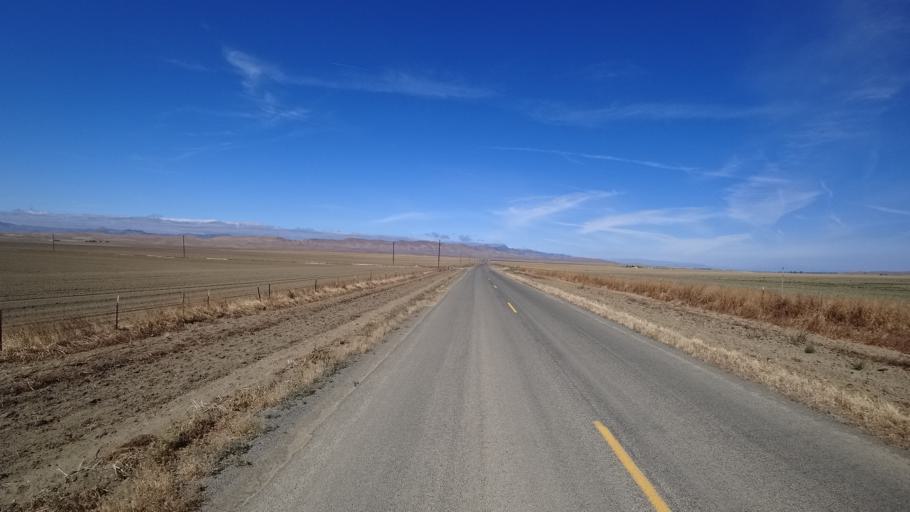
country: US
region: California
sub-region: Kings County
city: Kettleman City
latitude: 35.9351
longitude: -120.0383
